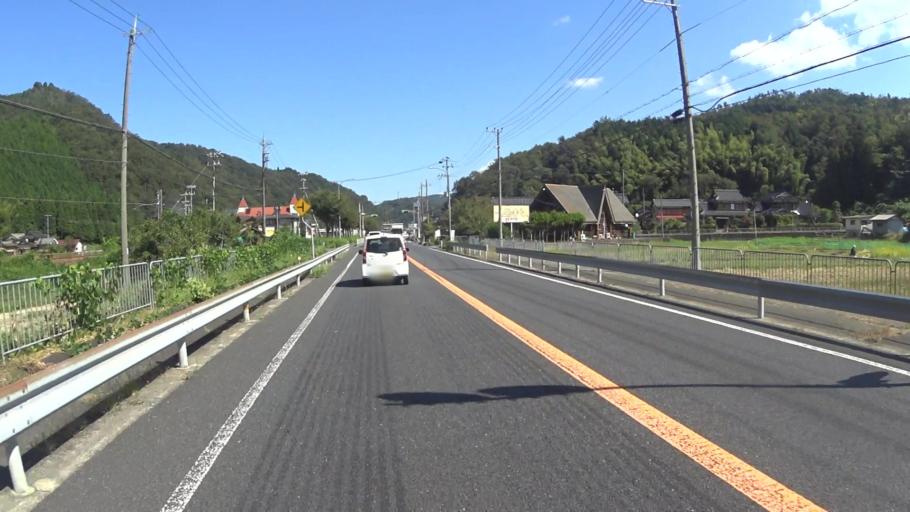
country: JP
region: Kyoto
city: Maizuru
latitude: 35.4035
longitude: 135.3236
